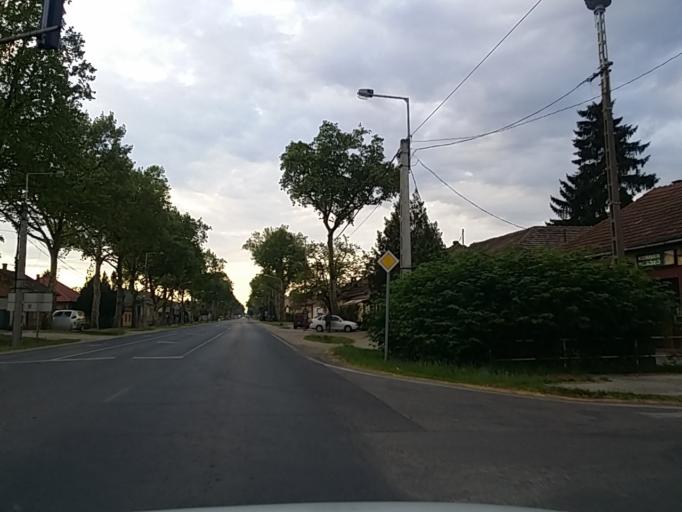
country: HU
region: Bacs-Kiskun
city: Lajosmizse
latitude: 47.0323
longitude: 19.5492
